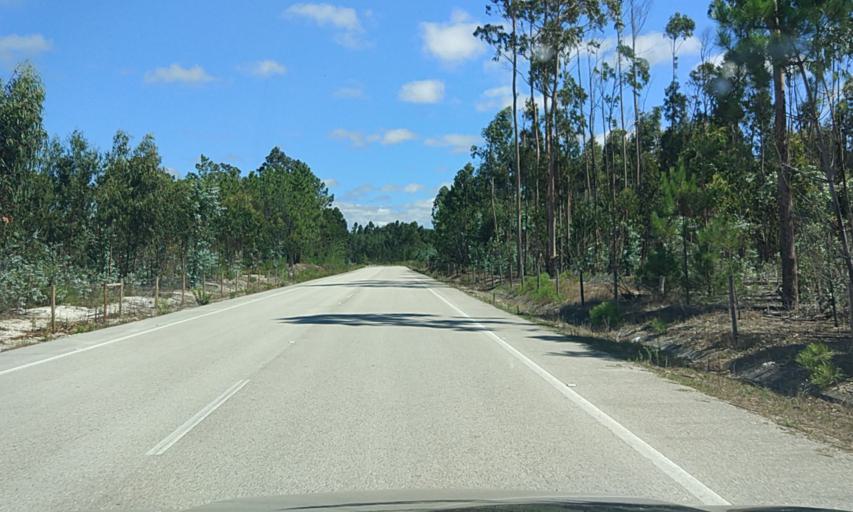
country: PT
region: Coimbra
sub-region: Mira
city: Mira
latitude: 40.3379
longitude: -8.7411
